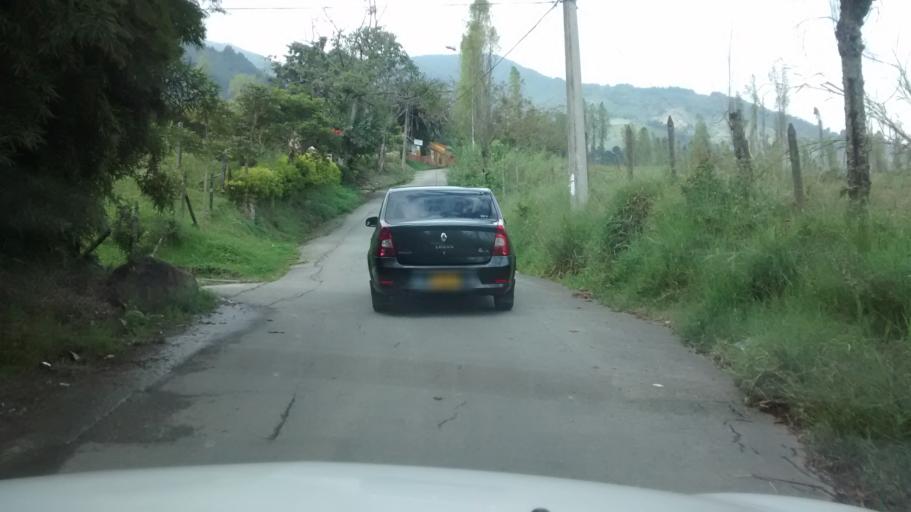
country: CO
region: Antioquia
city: La Estrella
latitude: 6.1744
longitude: -75.6615
